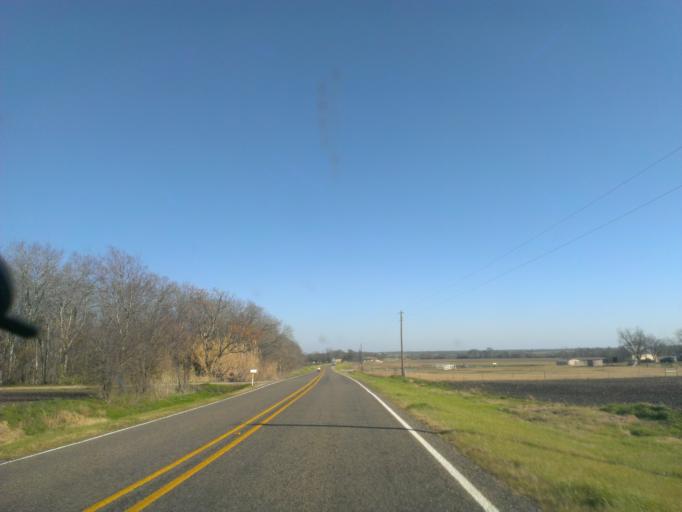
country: US
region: Texas
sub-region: Milam County
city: Thorndale
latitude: 30.5407
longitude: -97.2683
